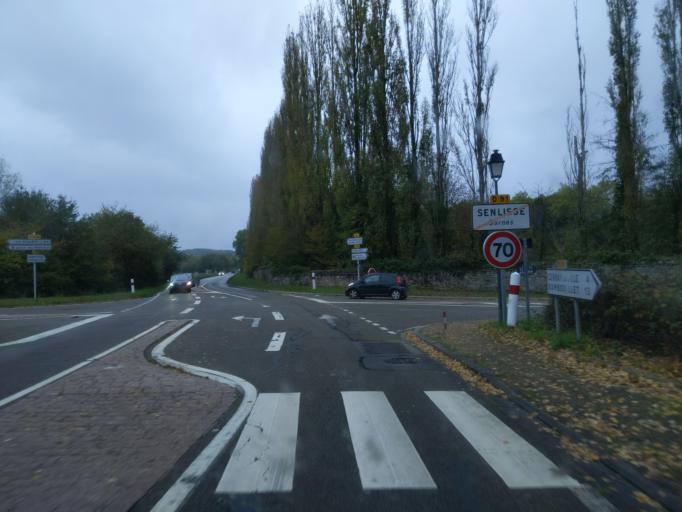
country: FR
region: Ile-de-France
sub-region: Departement des Yvelines
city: Dampierre-en-Yvelines
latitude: 48.6905
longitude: 1.9744
